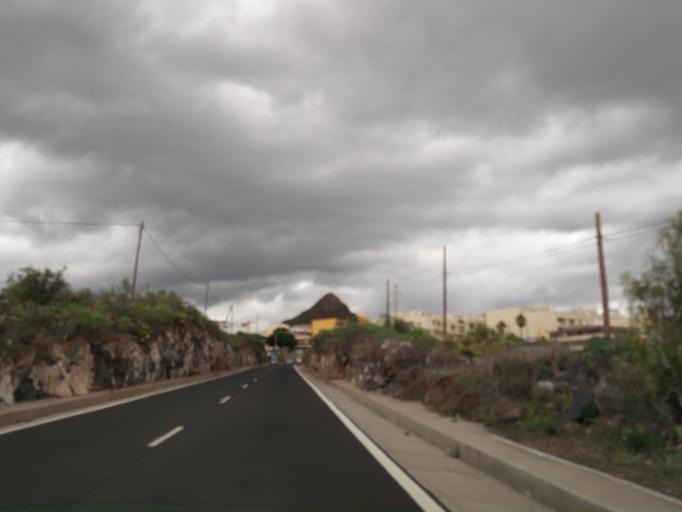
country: ES
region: Canary Islands
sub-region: Provincia de Santa Cruz de Tenerife
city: Arona
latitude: 28.0776
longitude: -16.6859
